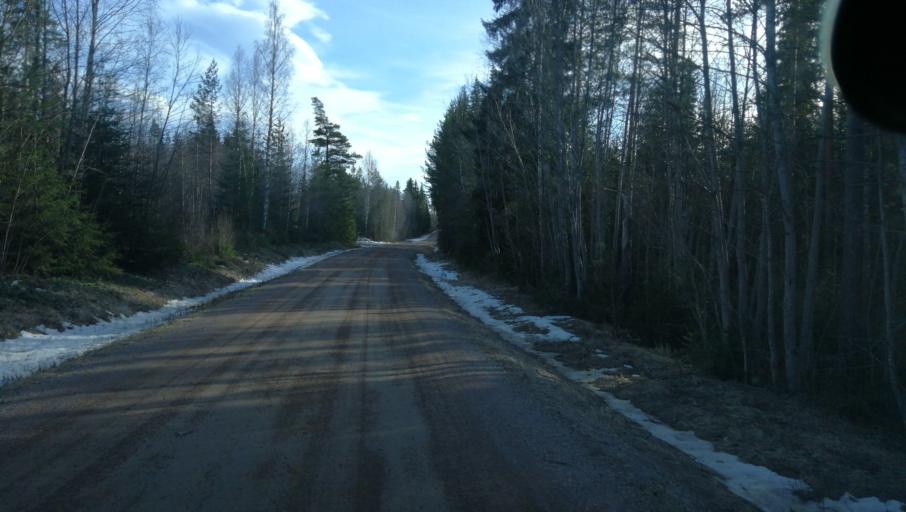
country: SE
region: Dalarna
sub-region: Vansbro Kommun
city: Vansbro
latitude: 60.8235
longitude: 14.1943
